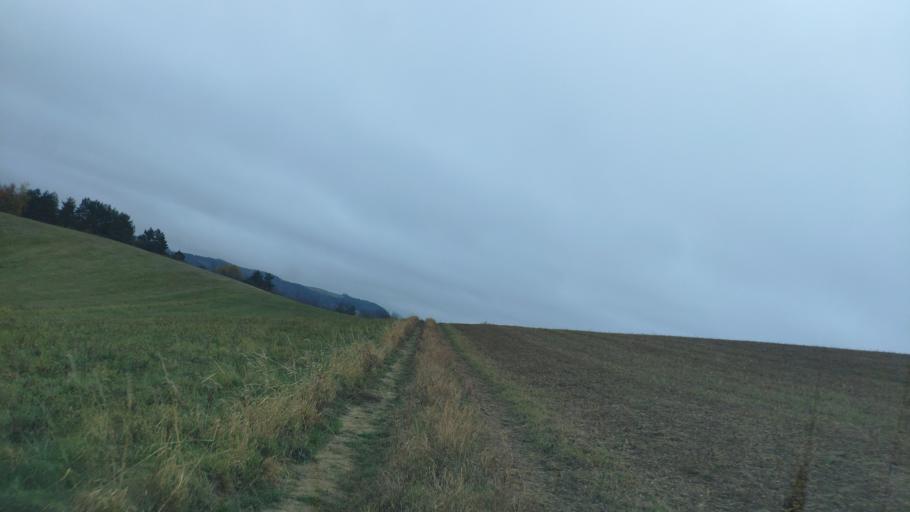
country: SK
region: Presovsky
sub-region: Okres Presov
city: Presov
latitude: 48.9315
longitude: 21.0926
